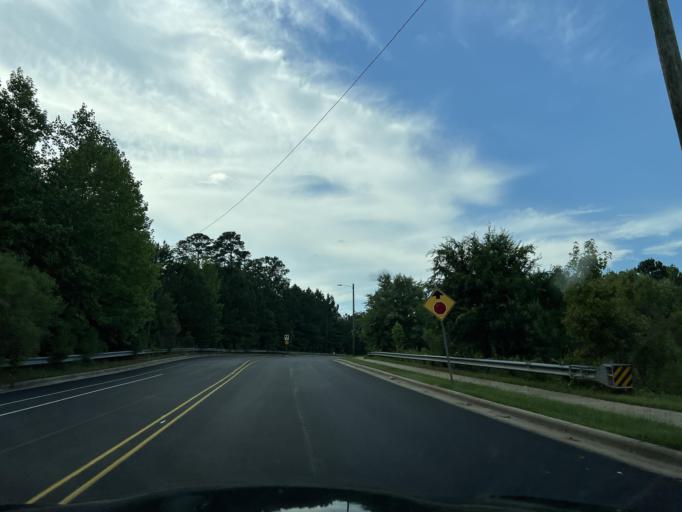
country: US
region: North Carolina
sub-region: Wake County
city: Morrisville
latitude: 35.9162
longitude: -78.7912
